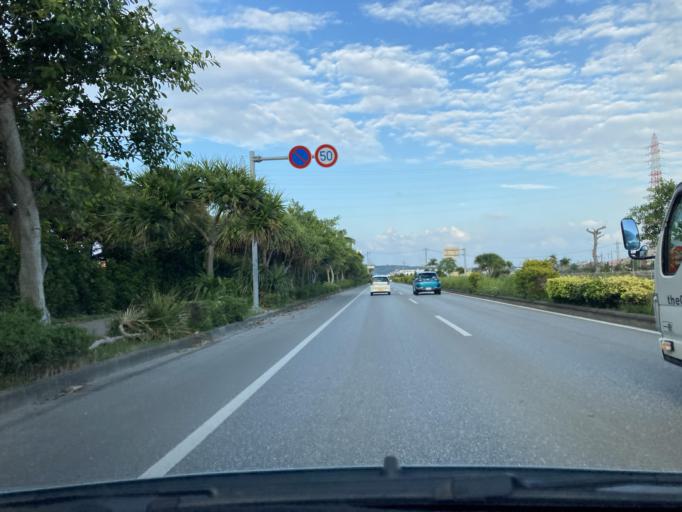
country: JP
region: Okinawa
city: Katsuren-haebaru
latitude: 26.3337
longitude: 127.8407
